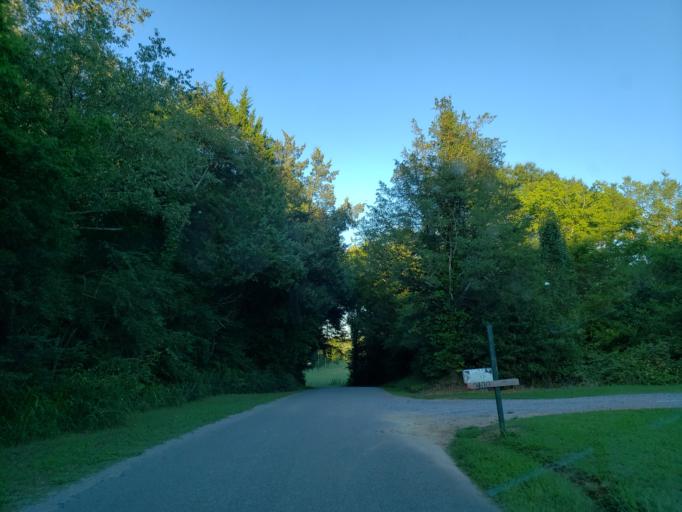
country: US
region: Georgia
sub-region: Bartow County
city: Euharlee
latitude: 34.0811
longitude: -84.9135
